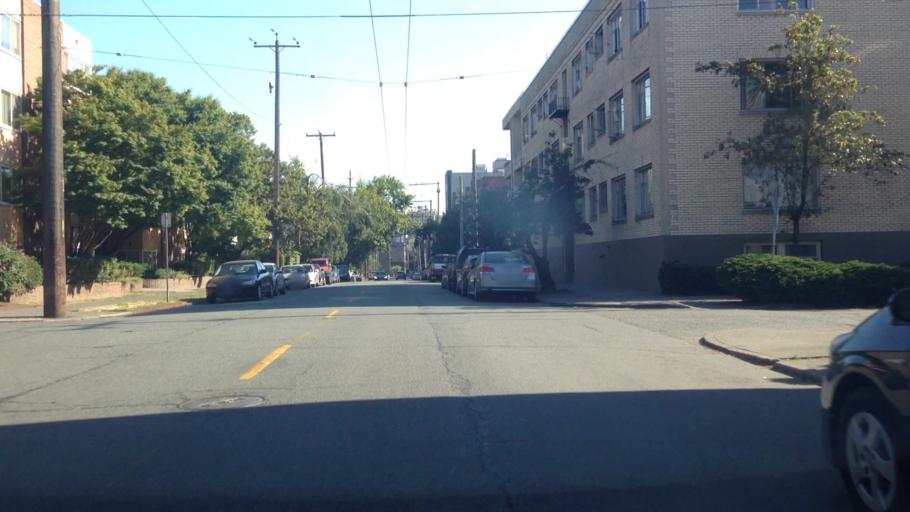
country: US
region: Washington
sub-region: King County
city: Seattle
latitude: 47.6222
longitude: -122.3266
